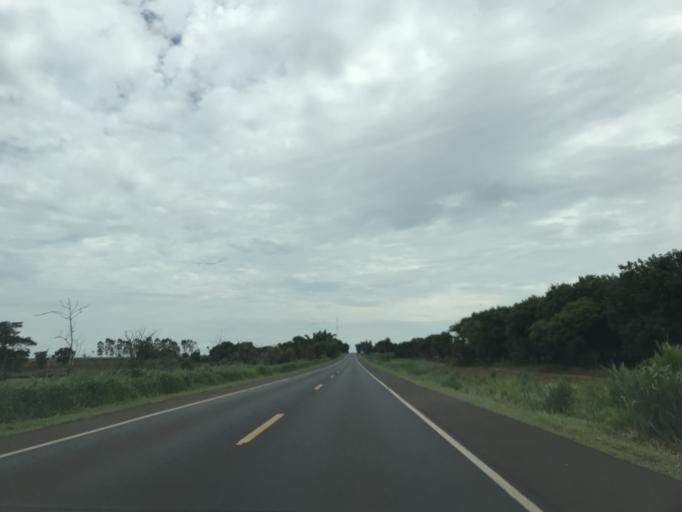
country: BR
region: Minas Gerais
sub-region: Frutal
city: Frutal
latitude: -20.1578
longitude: -49.1121
